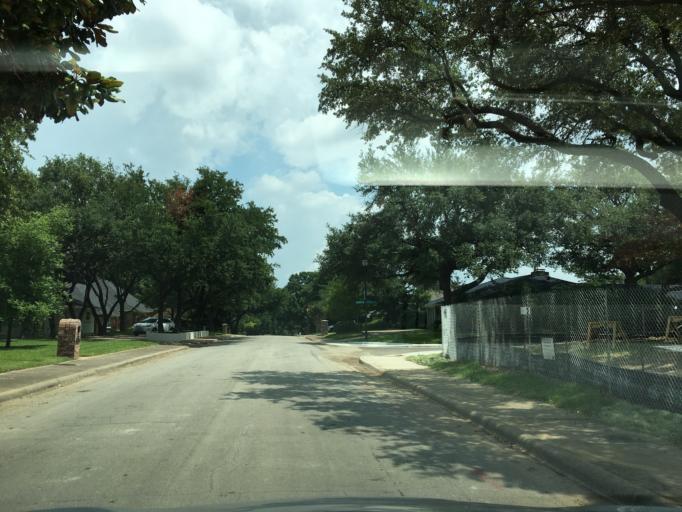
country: US
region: Texas
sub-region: Dallas County
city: University Park
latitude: 32.8928
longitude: -96.7837
